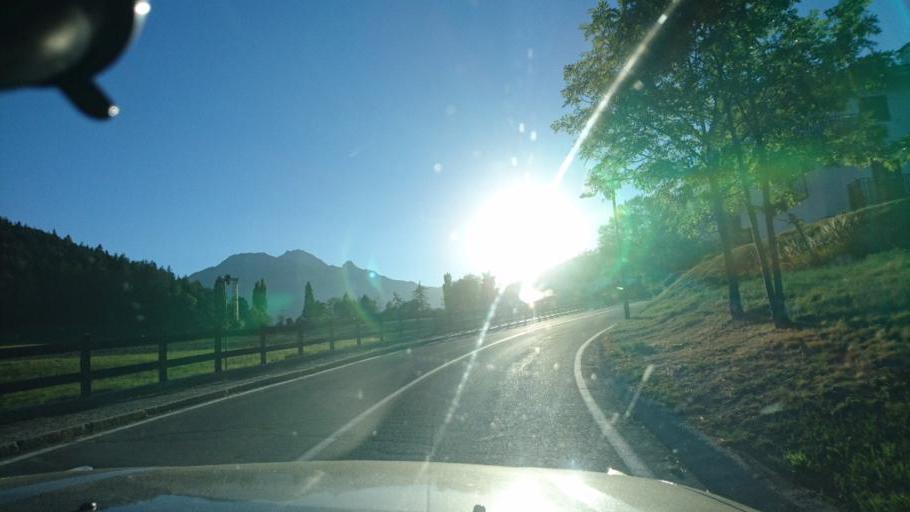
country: IT
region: Aosta Valley
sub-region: Valle d'Aosta
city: Saint-Nicolas
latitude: 45.7150
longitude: 7.1700
